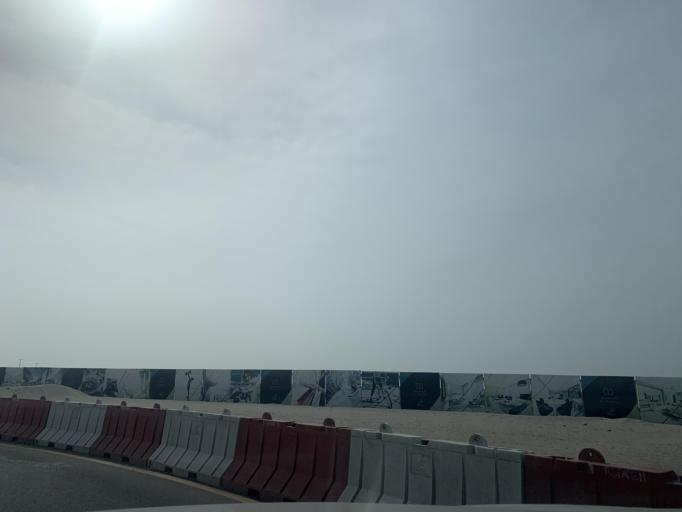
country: BH
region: Muharraq
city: Al Muharraq
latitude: 26.3127
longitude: 50.6431
